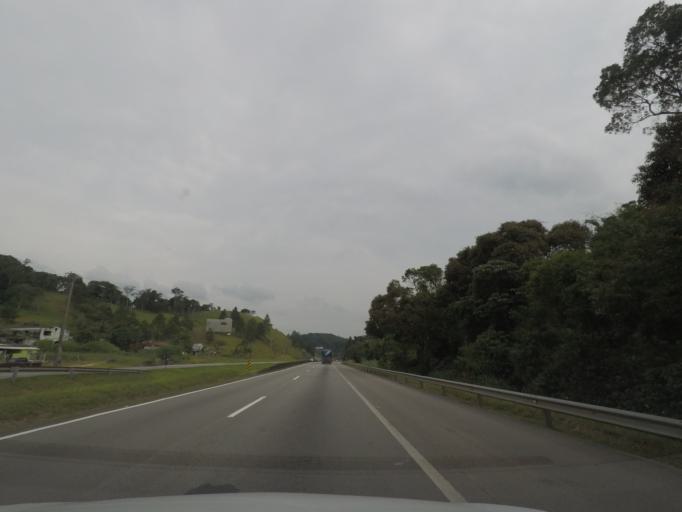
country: BR
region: Sao Paulo
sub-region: Juquitiba
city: Juquitiba
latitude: -23.9409
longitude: -47.0913
